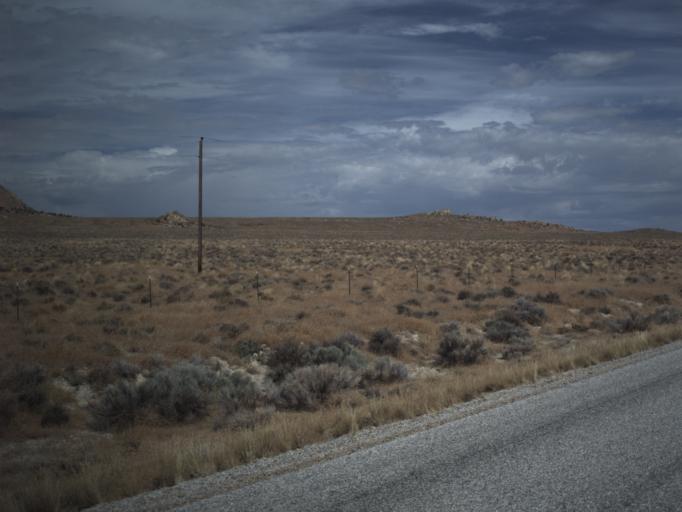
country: US
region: Utah
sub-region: Tooele County
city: Wendover
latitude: 41.4800
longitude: -113.6304
